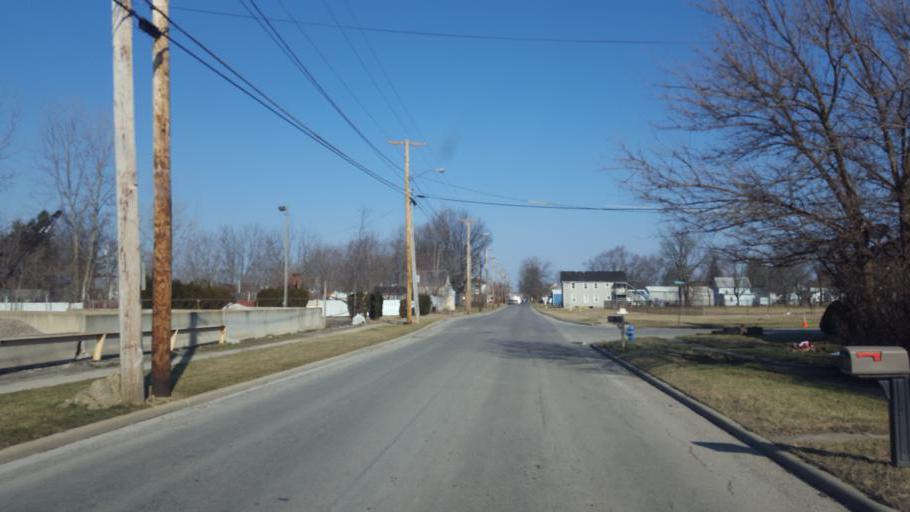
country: US
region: Ohio
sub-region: Crawford County
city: Galion
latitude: 40.7290
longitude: -82.7835
